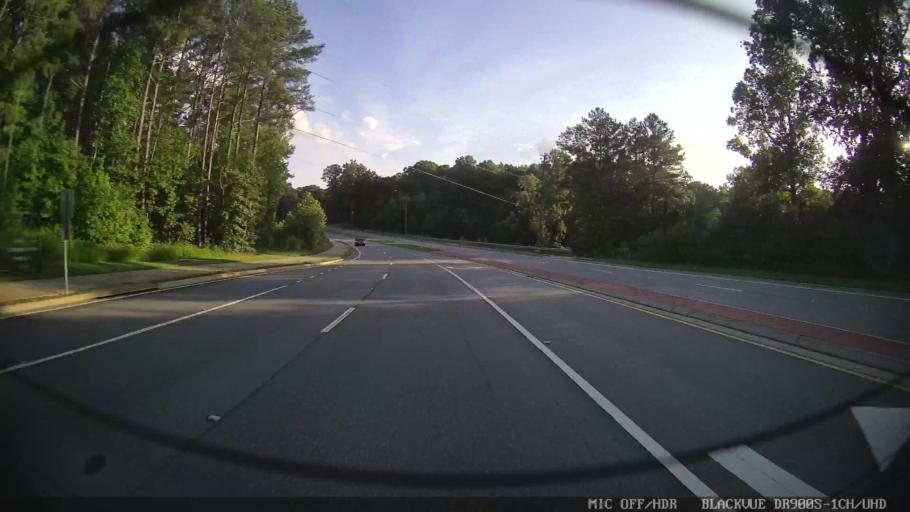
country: US
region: Georgia
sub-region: Fulton County
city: Milton
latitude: 34.1487
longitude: -84.2326
